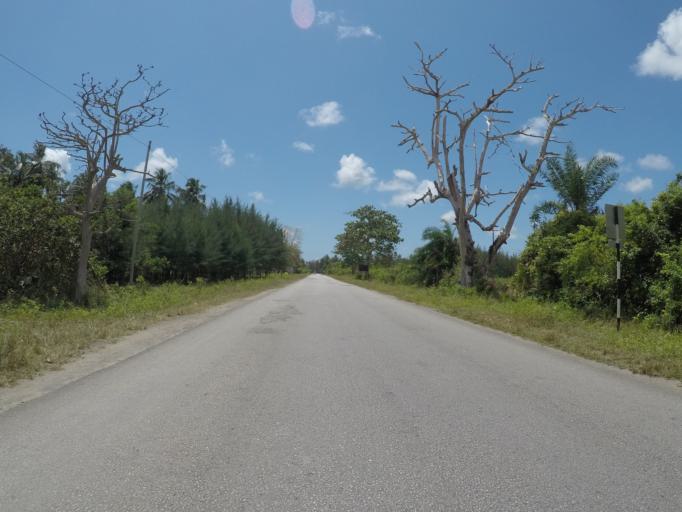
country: TZ
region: Zanzibar Central/South
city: Nganane
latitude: -6.2712
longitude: 39.4225
